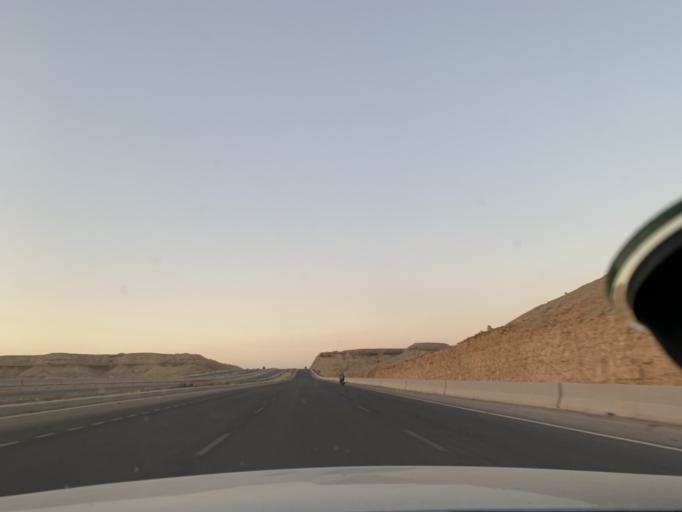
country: EG
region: Muhafazat al Qahirah
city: Halwan
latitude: 29.9451
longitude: 31.5346
